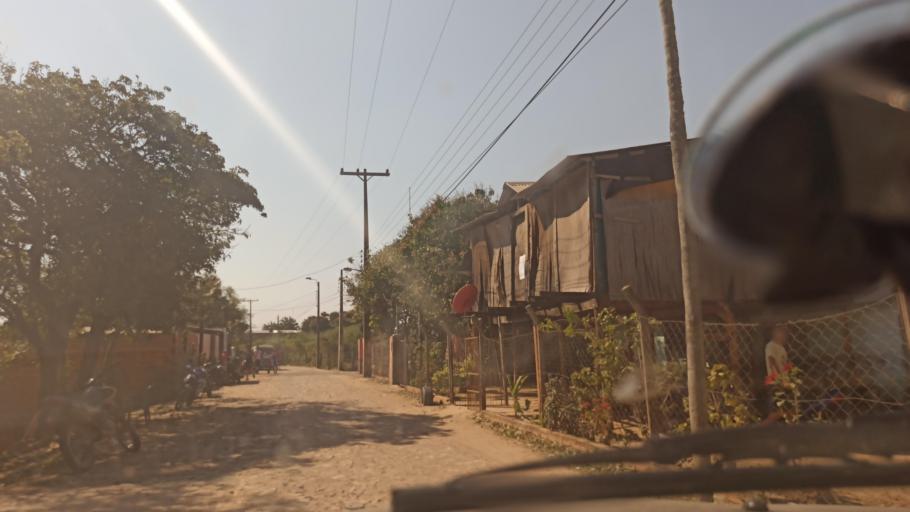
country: AR
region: Formosa
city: Clorinda
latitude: -25.2882
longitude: -57.6944
